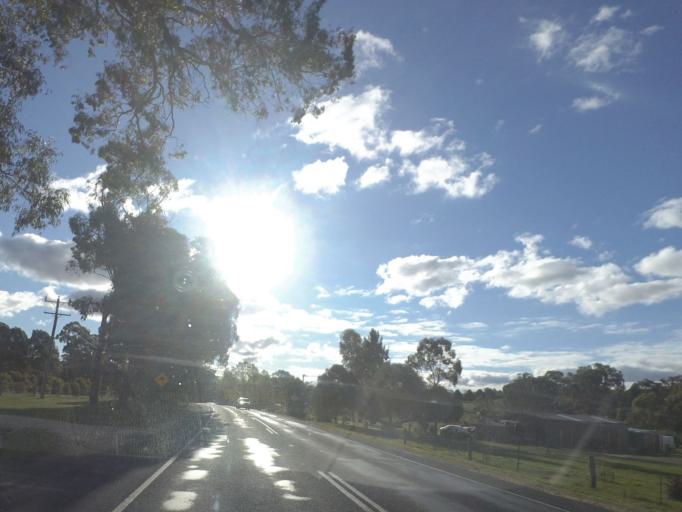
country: AU
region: Victoria
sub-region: Mount Alexander
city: Castlemaine
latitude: -37.0943
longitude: 144.2882
